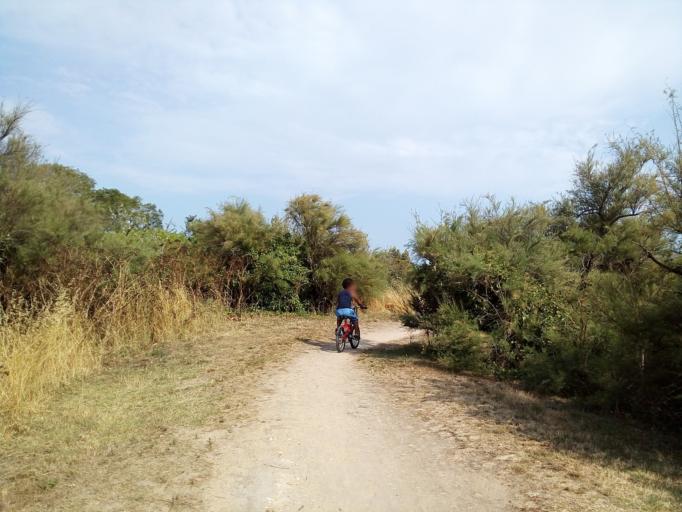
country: FR
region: Poitou-Charentes
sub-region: Departement de la Charente-Maritime
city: Boyard-Ville
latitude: 45.9538
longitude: -1.2429
